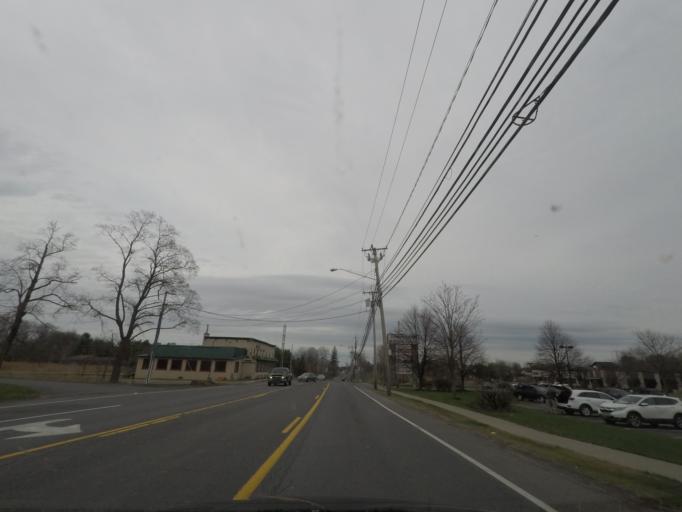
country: US
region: New York
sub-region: Albany County
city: Delmar
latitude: 42.6026
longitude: -73.7916
